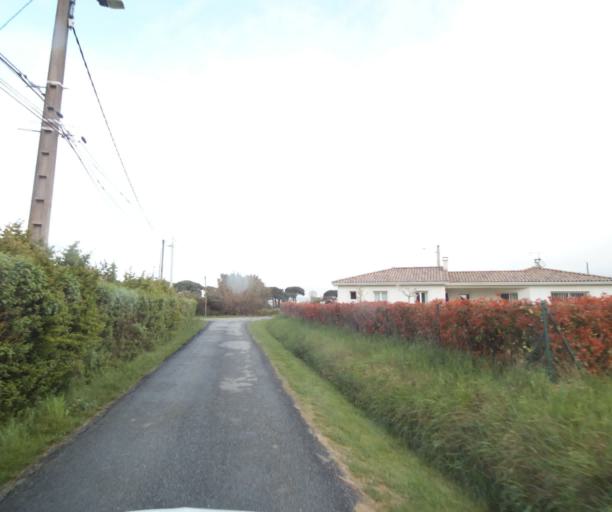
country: FR
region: Midi-Pyrenees
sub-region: Departement de l'Ariege
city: Saverdun
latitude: 43.2295
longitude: 1.5842
